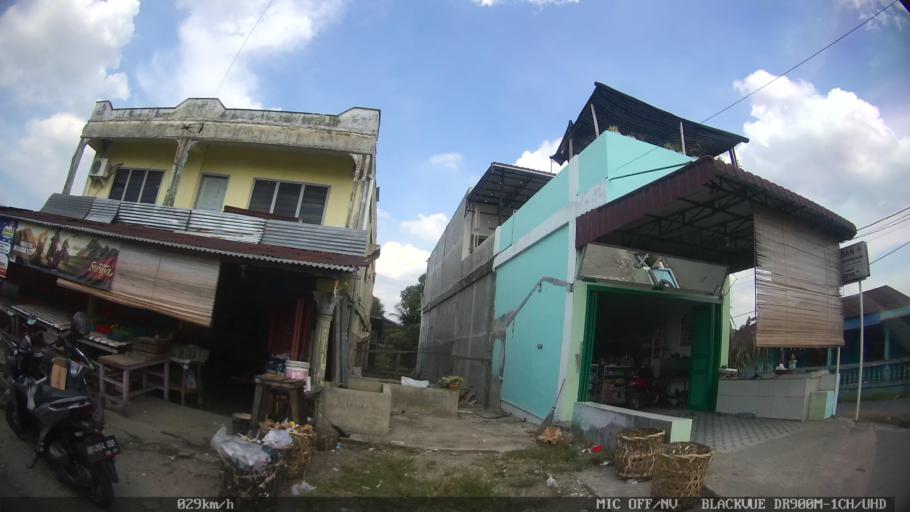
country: ID
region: North Sumatra
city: Binjai
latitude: 3.6290
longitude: 98.5019
